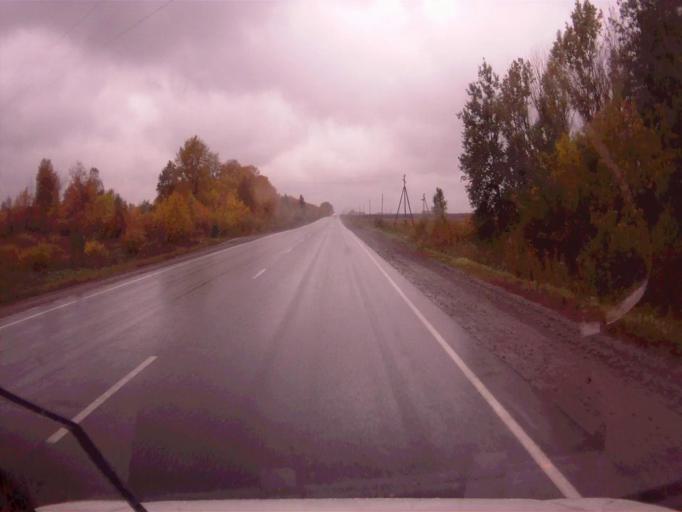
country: RU
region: Chelyabinsk
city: Argayash
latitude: 55.4246
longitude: 61.0061
